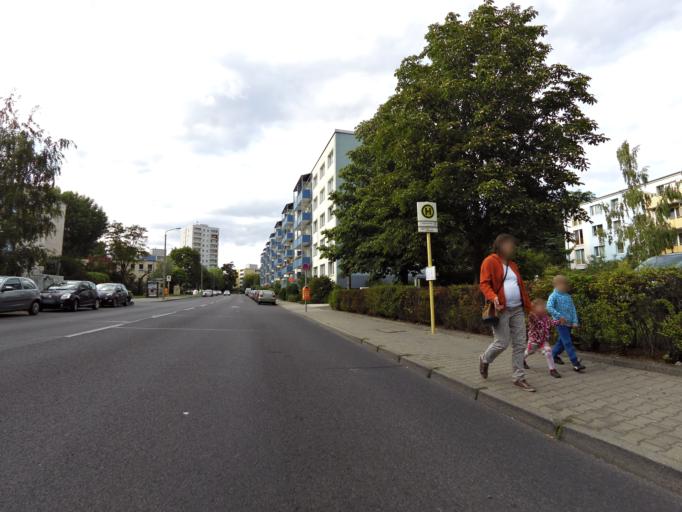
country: DE
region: Berlin
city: Johannisthal
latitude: 52.4393
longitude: 13.5015
